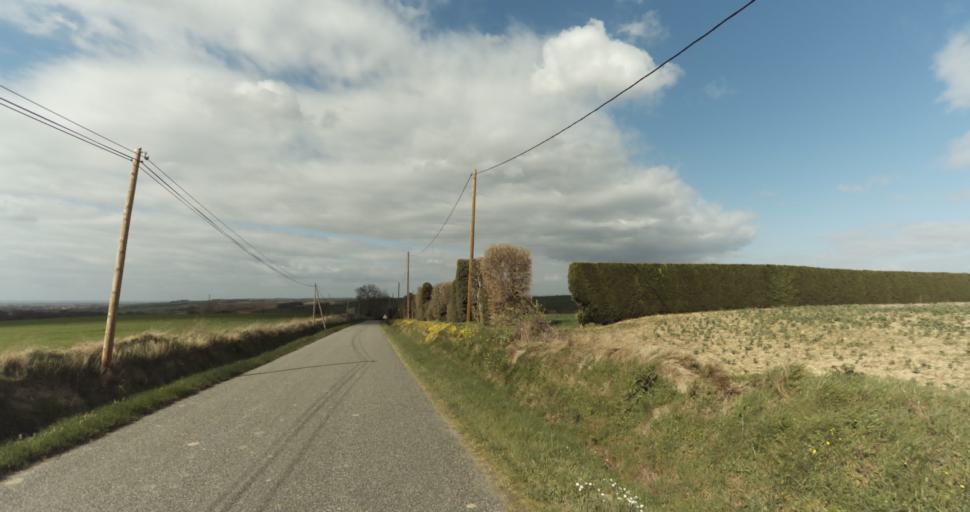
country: FR
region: Midi-Pyrenees
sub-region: Departement de la Haute-Garonne
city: Auterive
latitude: 43.3711
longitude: 1.4842
